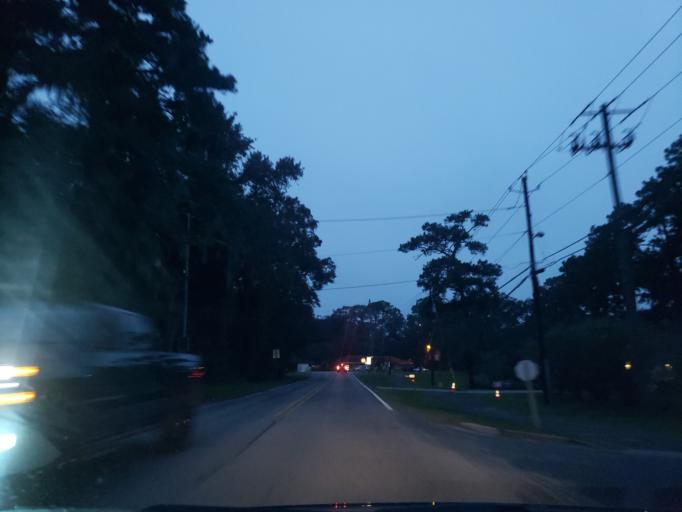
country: US
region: Georgia
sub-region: Chatham County
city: Wilmington Island
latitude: 32.0234
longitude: -80.9658
